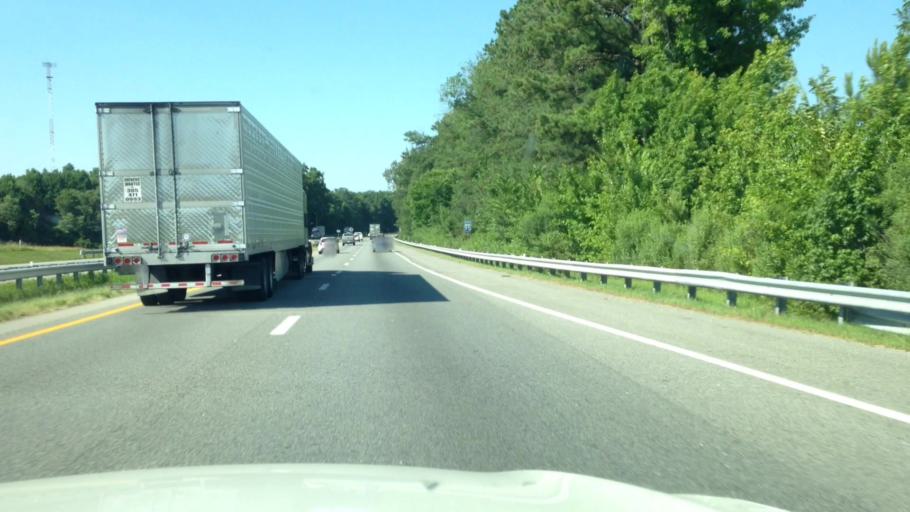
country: US
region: Virginia
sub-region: City of Emporia
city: Emporia
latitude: 36.7069
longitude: -77.5470
